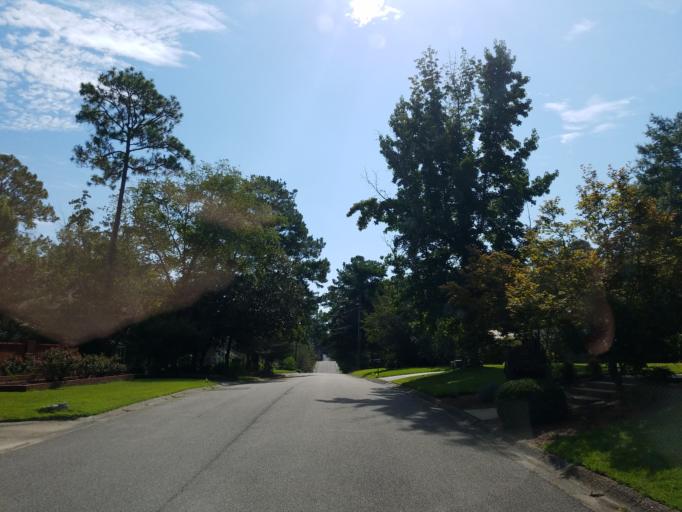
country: US
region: Mississippi
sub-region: Lamar County
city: West Hattiesburg
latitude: 31.3142
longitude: -89.3438
